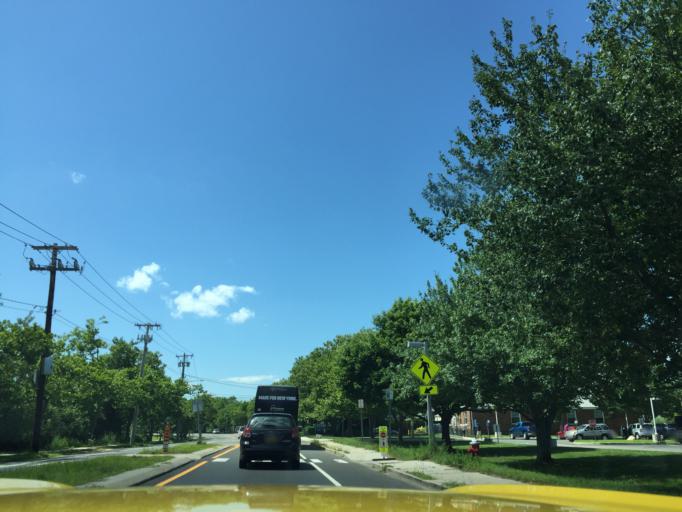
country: US
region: New York
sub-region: Suffolk County
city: Amagansett
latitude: 40.9789
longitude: -72.1278
